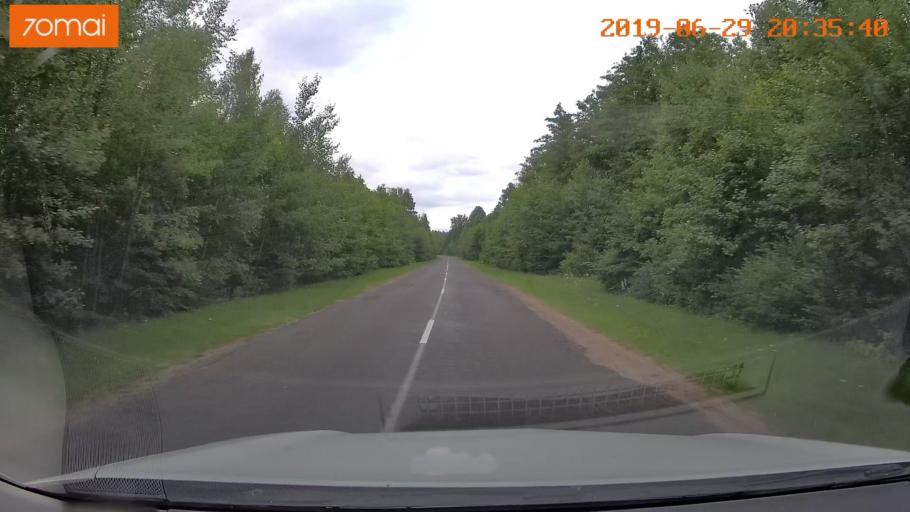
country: BY
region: Brest
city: Hantsavichy
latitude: 52.5182
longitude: 26.3522
